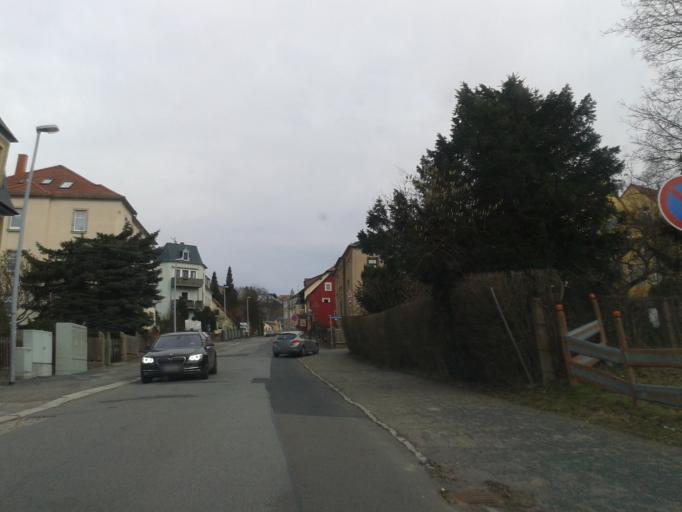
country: DE
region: Saxony
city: Freital
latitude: 51.0119
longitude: 13.6777
